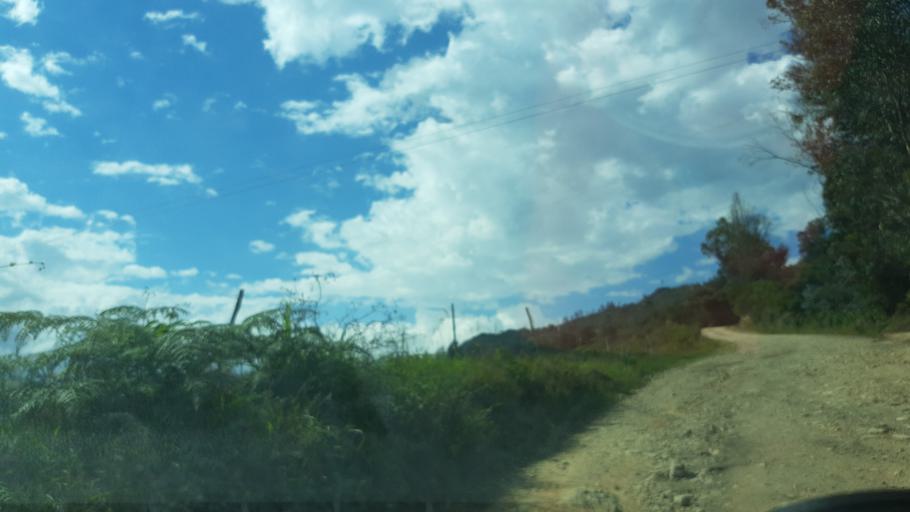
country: CO
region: Boyaca
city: Santa Sofia
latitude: 5.7203
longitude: -73.5403
